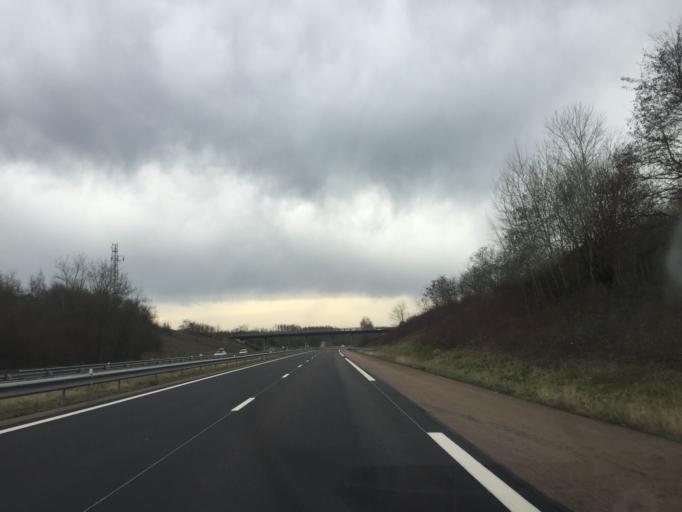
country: FR
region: Franche-Comte
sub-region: Departement du Jura
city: Bletterans
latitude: 46.7300
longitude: 5.5075
